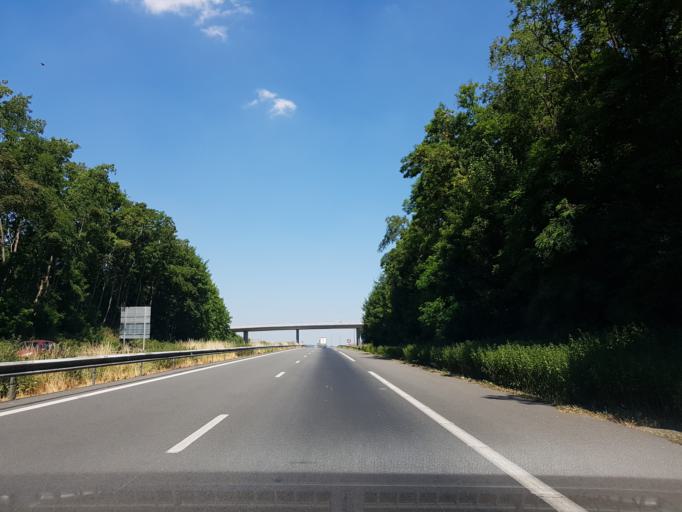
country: FR
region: Nord-Pas-de-Calais
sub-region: Departement du Nord
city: Marcoing
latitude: 50.0912
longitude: 3.1708
